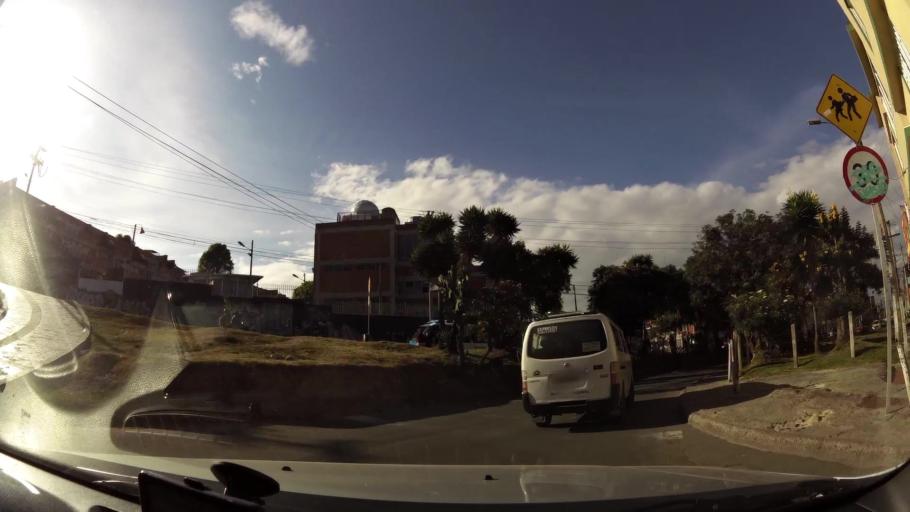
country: CO
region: Cundinamarca
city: Soacha
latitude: 4.5704
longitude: -74.1526
